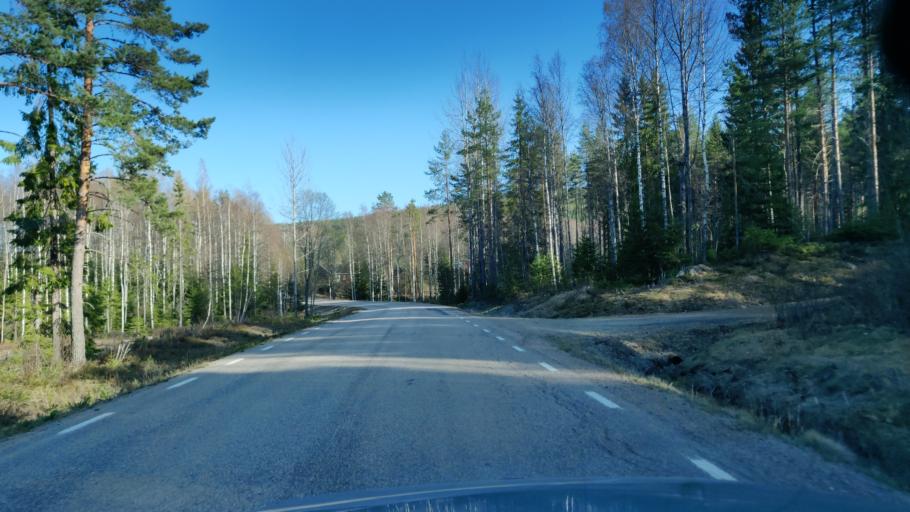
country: SE
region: Vaermland
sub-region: Hagfors Kommun
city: Ekshaerad
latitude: 59.9831
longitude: 13.3565
